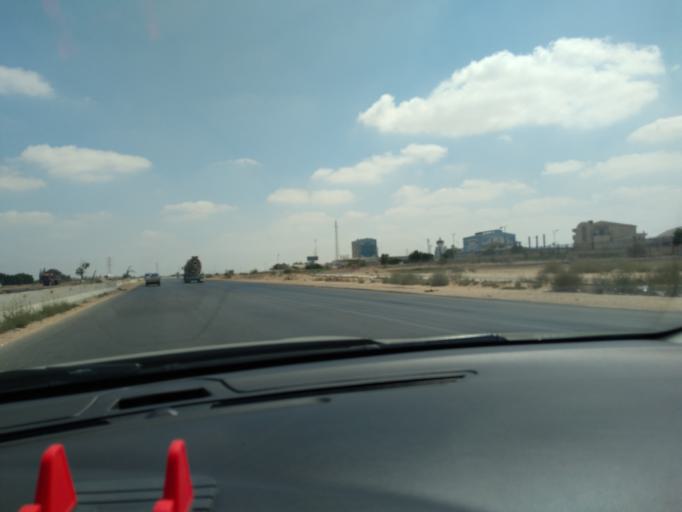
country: EG
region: Al Isma'iliyah
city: At Tall al Kabir
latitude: 30.3407
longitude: 31.8660
